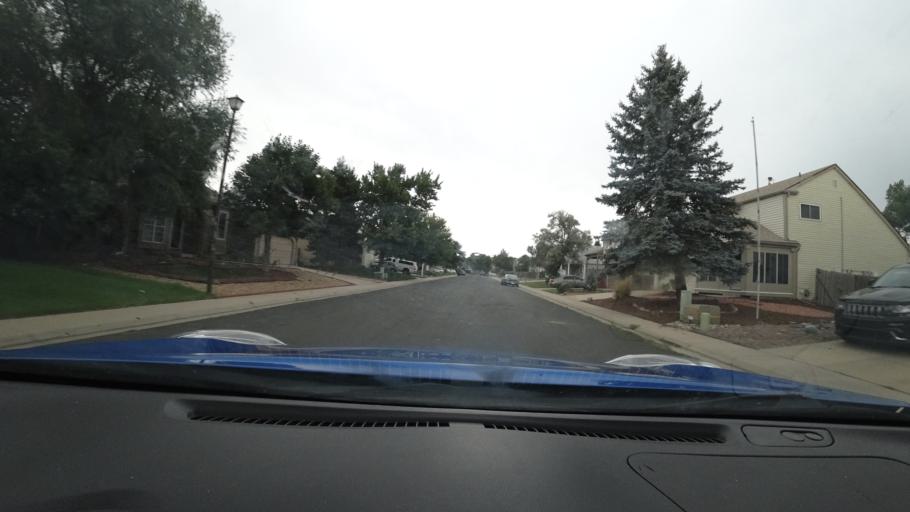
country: US
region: Colorado
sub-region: Adams County
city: Aurora
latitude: 39.7774
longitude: -104.7482
